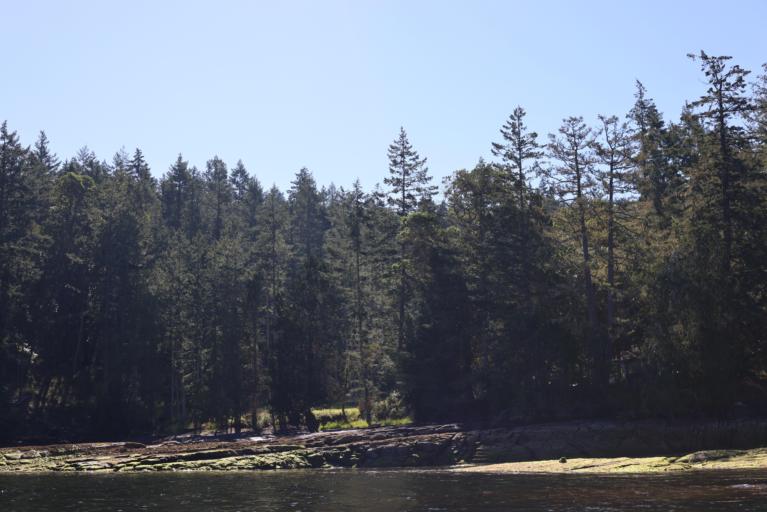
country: CA
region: British Columbia
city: North Cowichan
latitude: 48.8015
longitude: -123.5980
